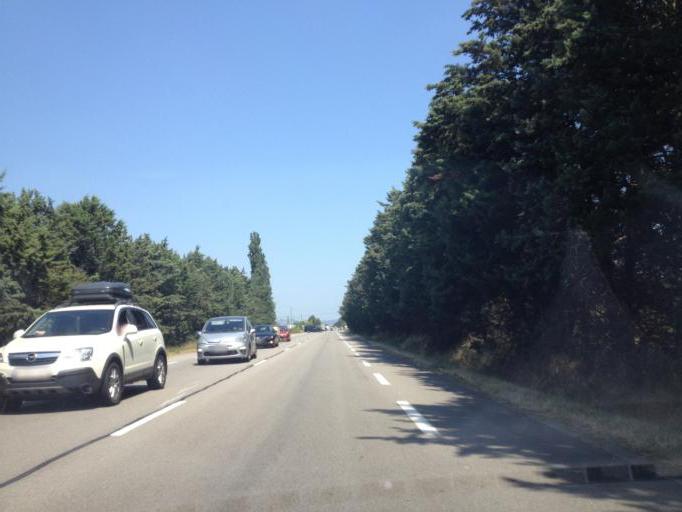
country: FR
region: Rhone-Alpes
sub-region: Departement de la Drome
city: Bourg-les-Valence
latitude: 44.9775
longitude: 4.8829
